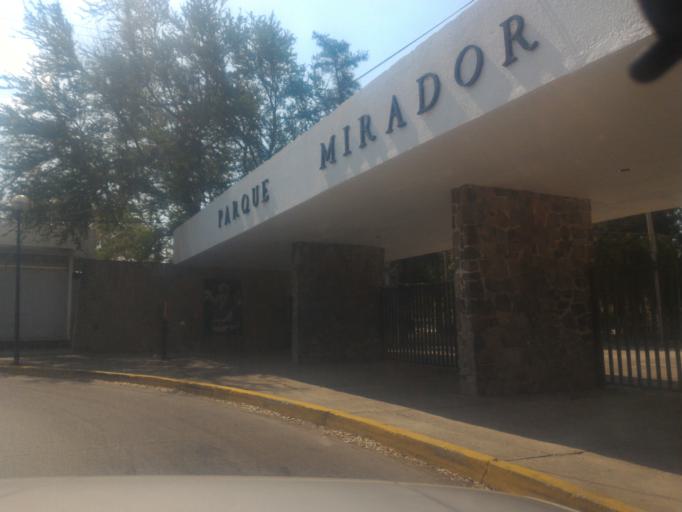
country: MX
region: Jalisco
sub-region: Zapopan
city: San Isidro
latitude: 20.7396
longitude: -103.3113
